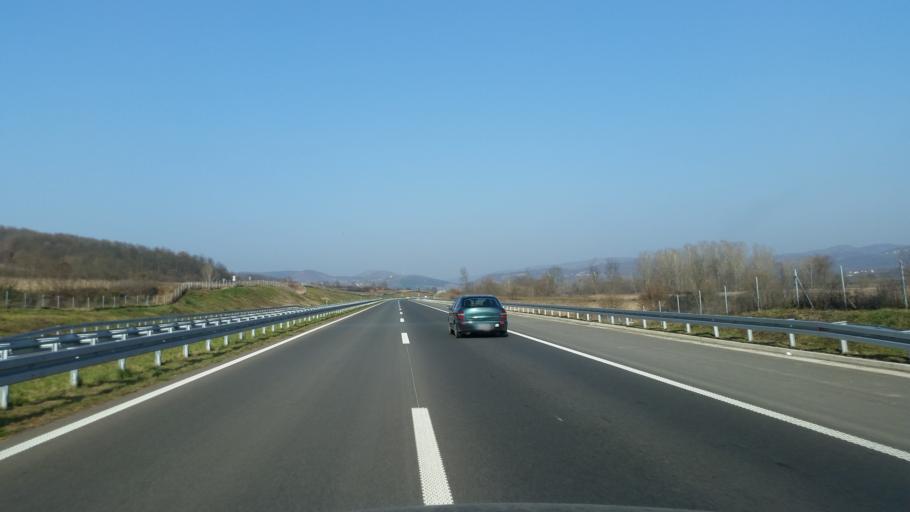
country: RS
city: Prislonica
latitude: 43.9397
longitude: 20.4006
